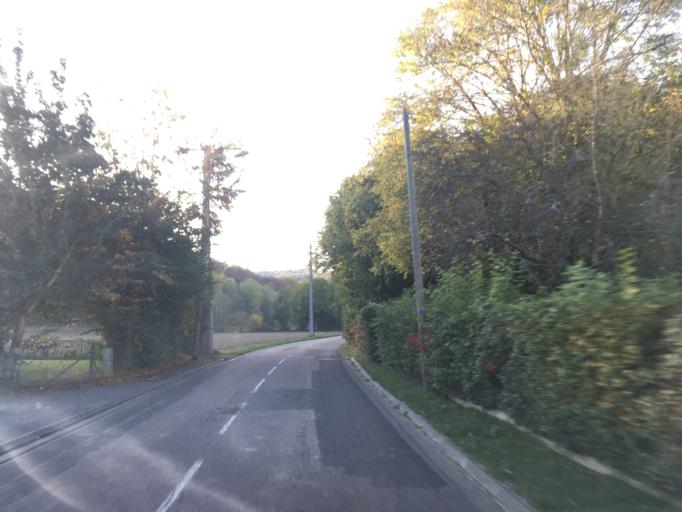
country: FR
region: Haute-Normandie
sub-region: Departement de l'Eure
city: Heudreville-sur-Eure
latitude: 49.1015
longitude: 1.2368
